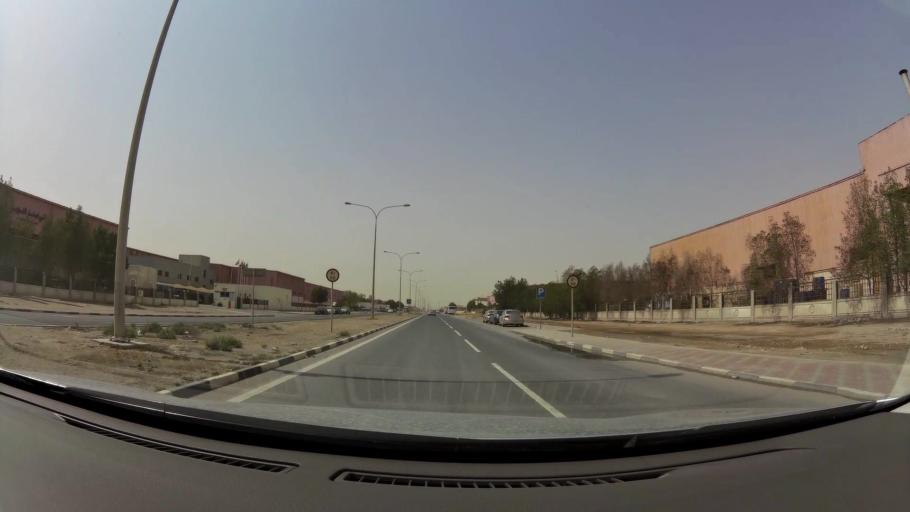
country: QA
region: Al Wakrah
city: Al Wukayr
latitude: 25.1563
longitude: 51.4098
